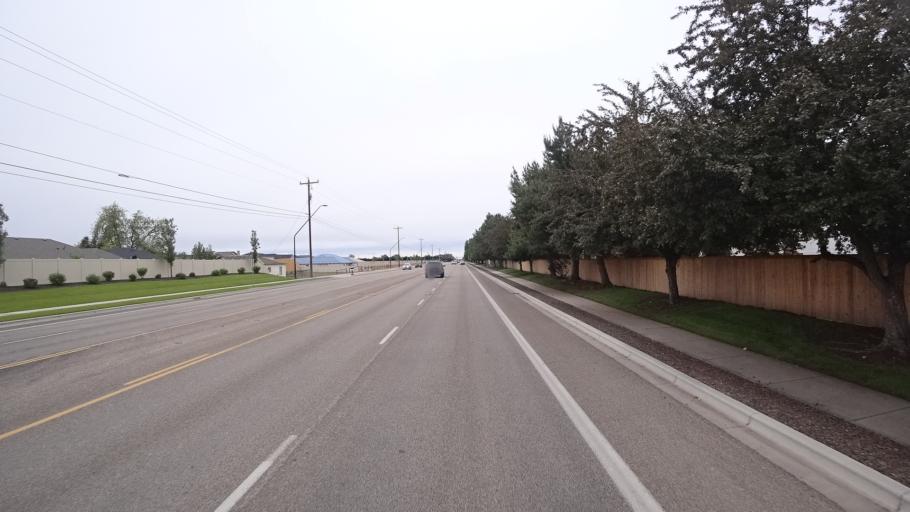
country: US
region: Idaho
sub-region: Ada County
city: Meridian
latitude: 43.6339
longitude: -116.3680
